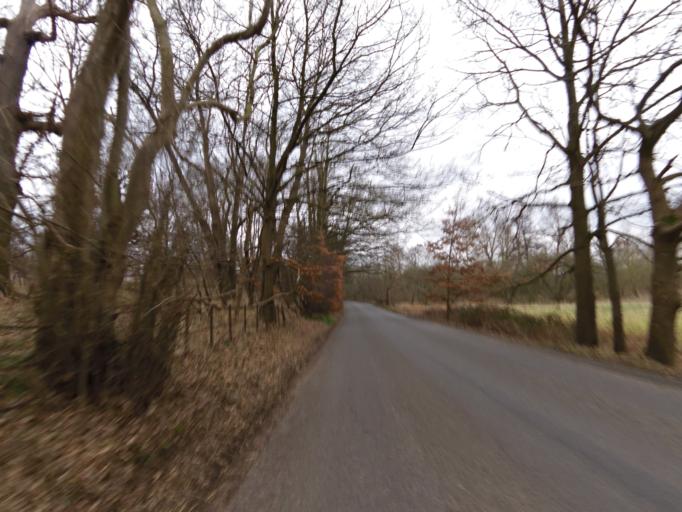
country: GB
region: England
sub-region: Suffolk
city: Wickham Market
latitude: 52.1666
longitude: 1.3561
